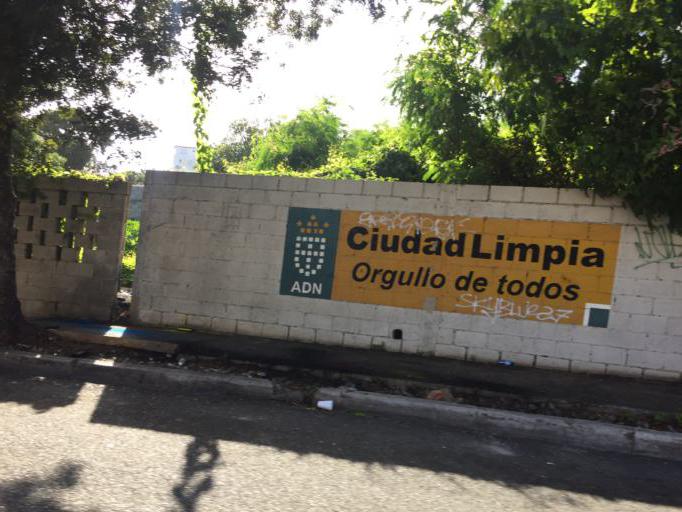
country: DO
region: Nacional
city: La Julia
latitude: 18.4602
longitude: -69.9223
